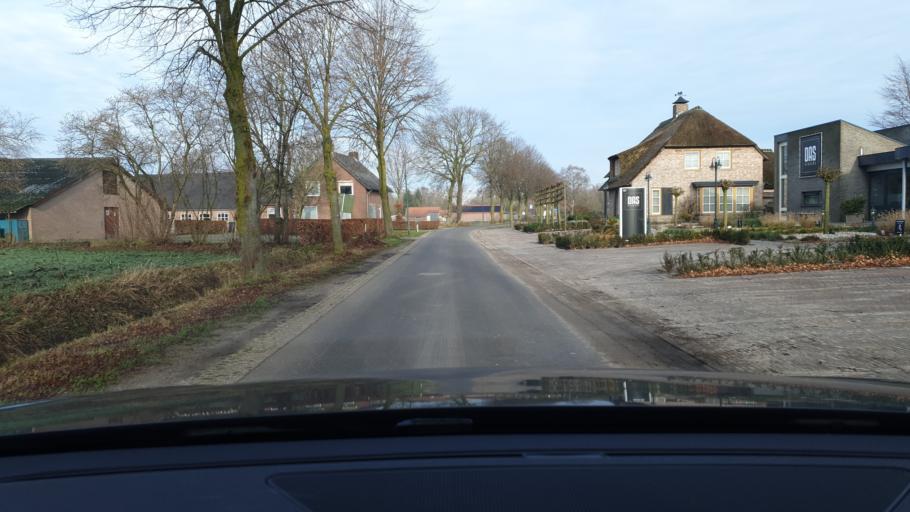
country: NL
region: North Brabant
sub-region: Gemeente Veldhoven
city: Oerle
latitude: 51.4387
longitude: 5.3429
